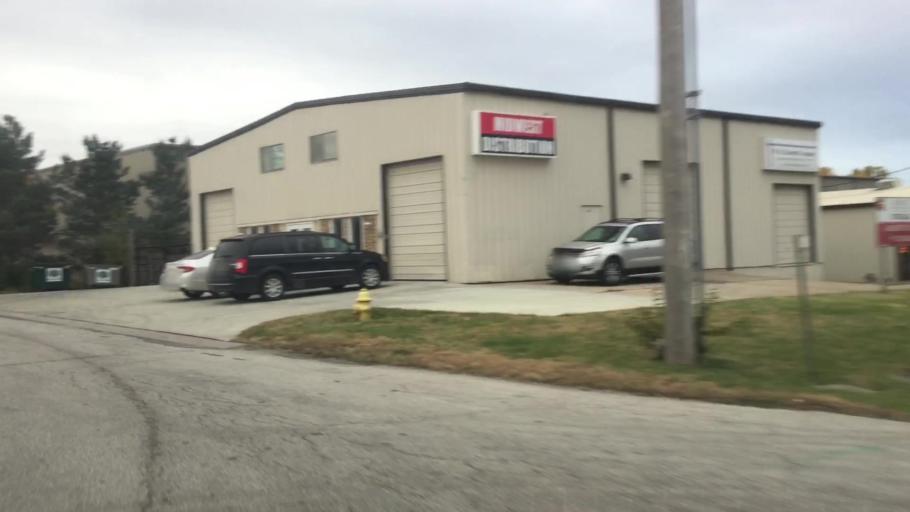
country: US
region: Missouri
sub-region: Jackson County
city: Lees Summit
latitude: 38.9026
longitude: -94.3688
